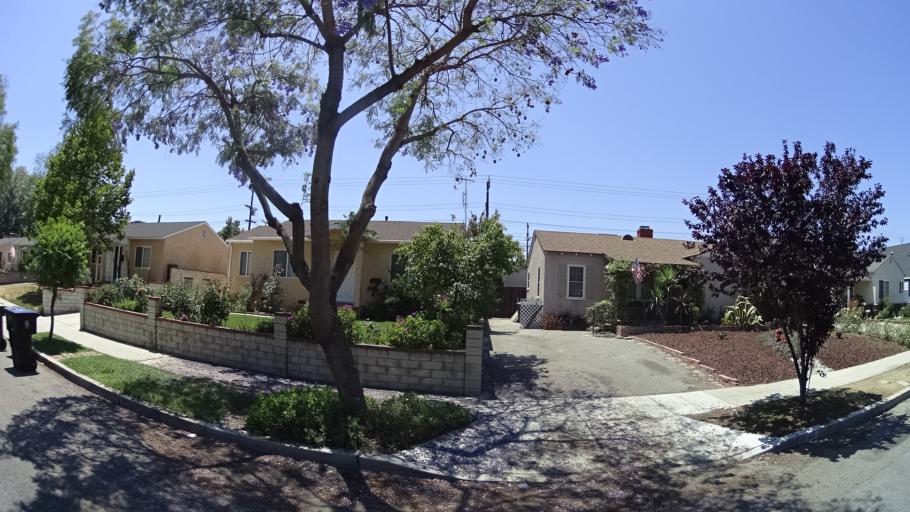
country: US
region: California
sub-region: Los Angeles County
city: North Hollywood
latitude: 34.1828
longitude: -118.3481
